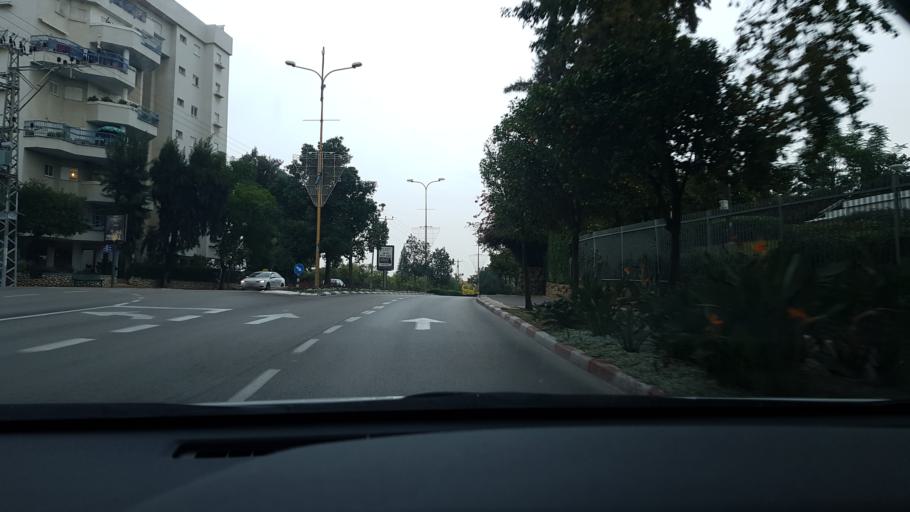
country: IL
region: Central District
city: Ness Ziona
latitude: 31.9043
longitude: 34.8072
